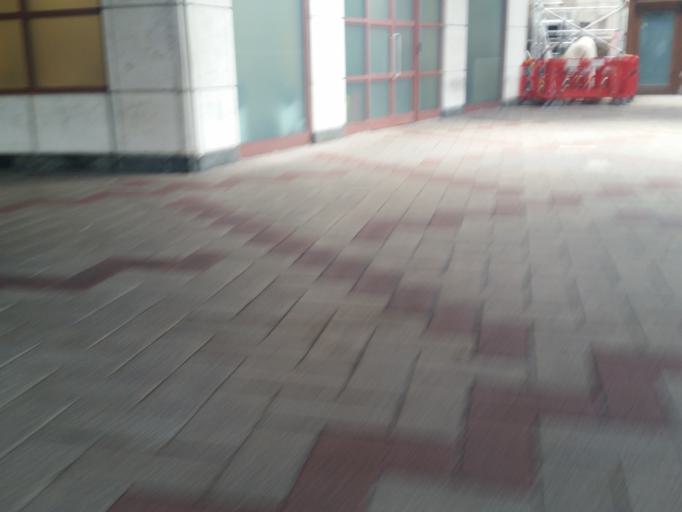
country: GB
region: England
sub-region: Greater London
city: Poplar
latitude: 51.5062
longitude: -0.0206
